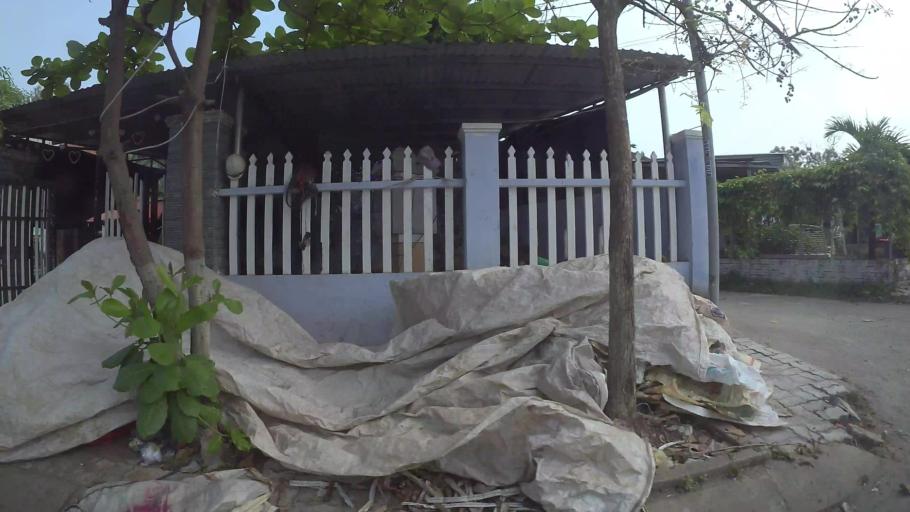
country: VN
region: Da Nang
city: Lien Chieu
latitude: 16.0484
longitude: 108.1475
